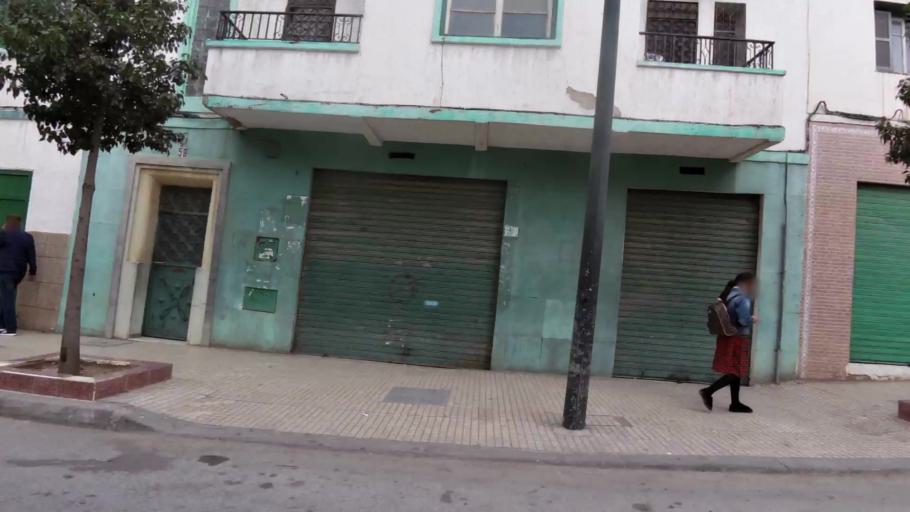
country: MA
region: Tanger-Tetouan
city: Tetouan
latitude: 35.5754
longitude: -5.3823
